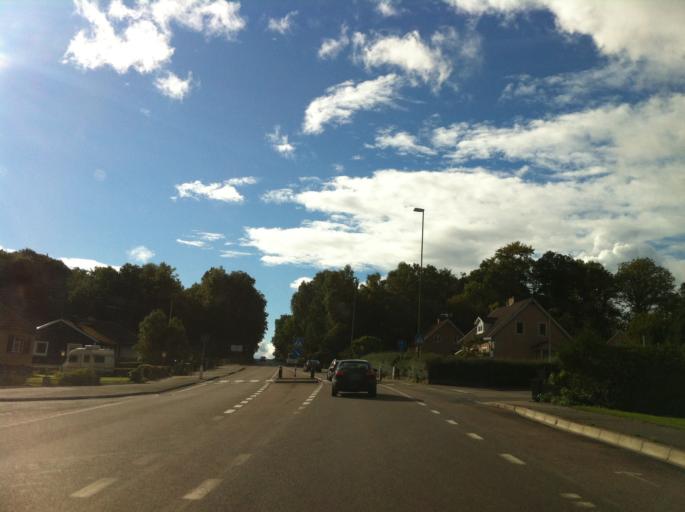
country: SE
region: Skane
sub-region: Hassleholms Kommun
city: Sosdala
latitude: 56.1634
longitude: 13.5891
